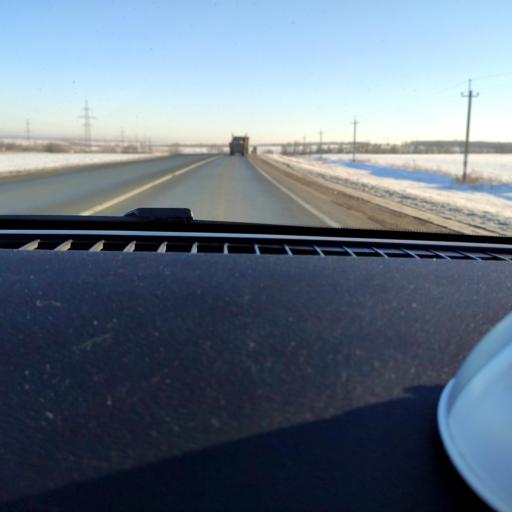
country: RU
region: Samara
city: Smyshlyayevka
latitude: 53.1480
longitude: 50.4976
